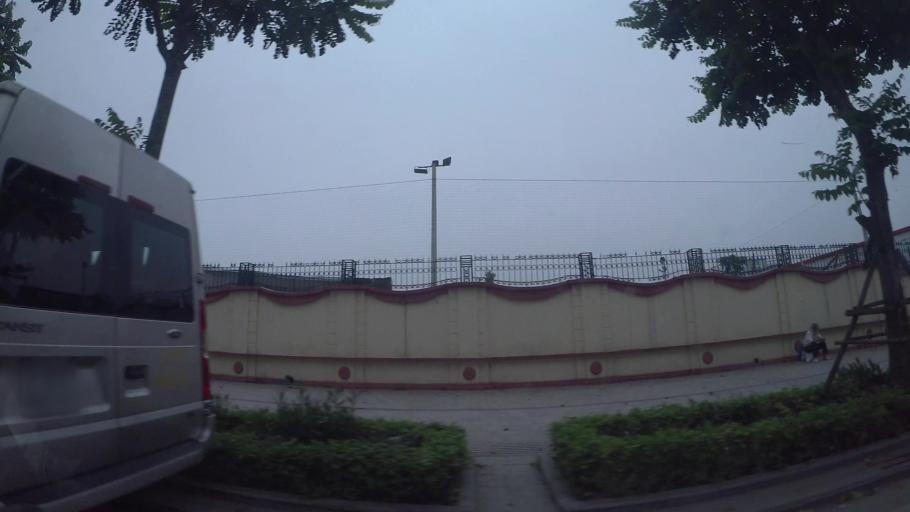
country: VN
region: Ha Noi
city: Hai BaTrung
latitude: 20.9920
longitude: 105.8328
